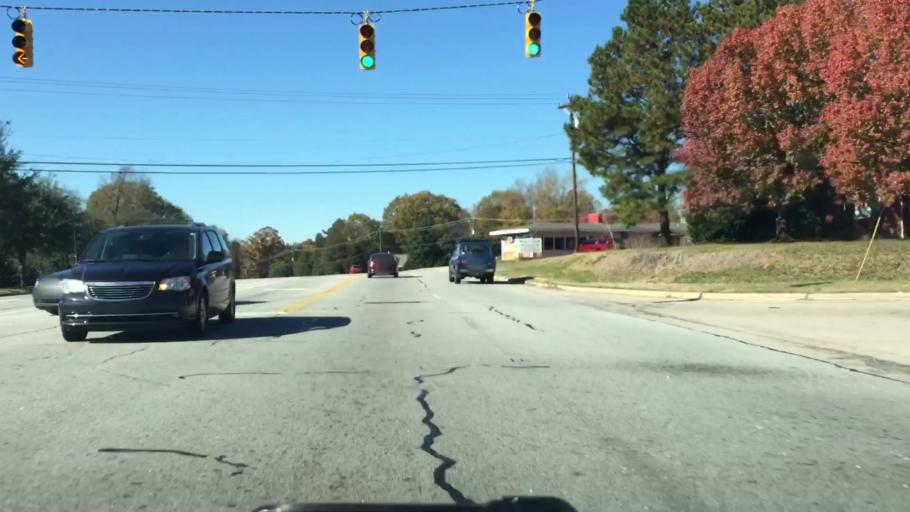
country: US
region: North Carolina
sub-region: Rowan County
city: Salisbury
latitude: 35.6632
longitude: -80.5042
